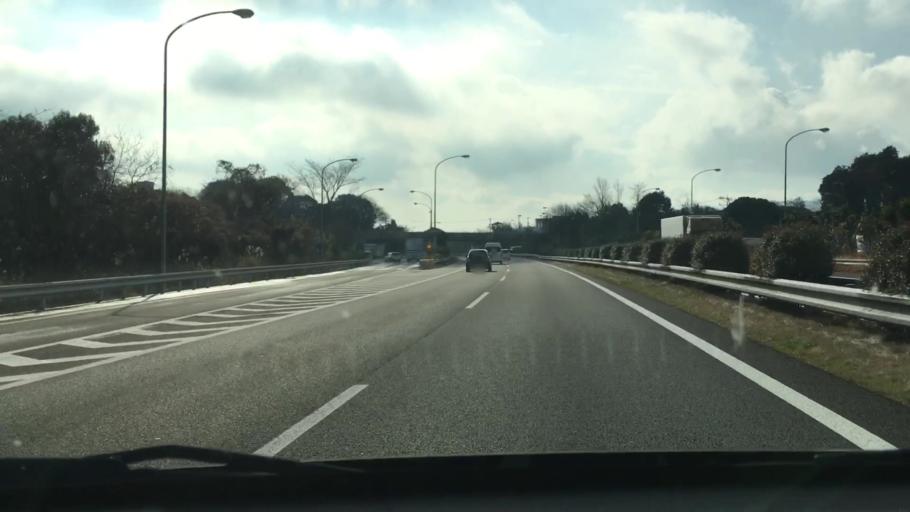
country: JP
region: Kumamoto
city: Uto
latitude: 32.7094
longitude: 130.7576
